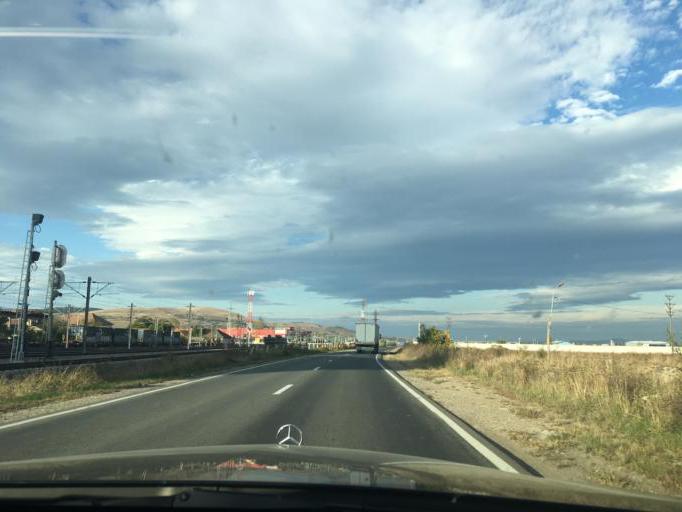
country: RO
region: Alba
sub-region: Municipiul Alba Iulia
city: Barabant
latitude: 46.0880
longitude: 23.5983
